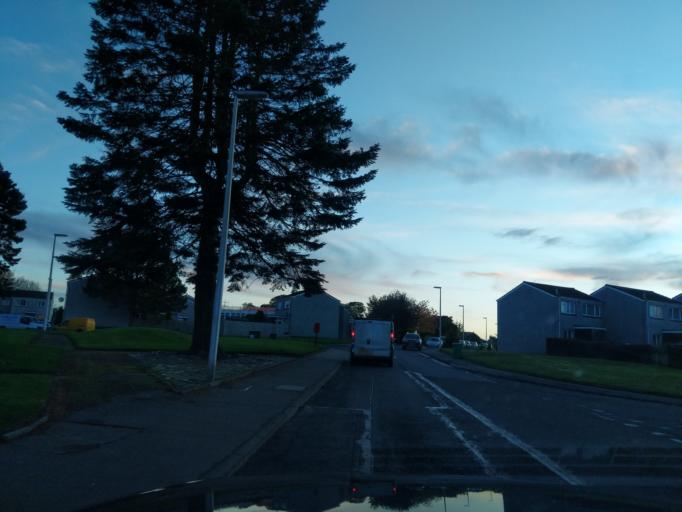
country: GB
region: Scotland
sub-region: Fife
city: Leuchars
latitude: 56.3842
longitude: -2.8799
